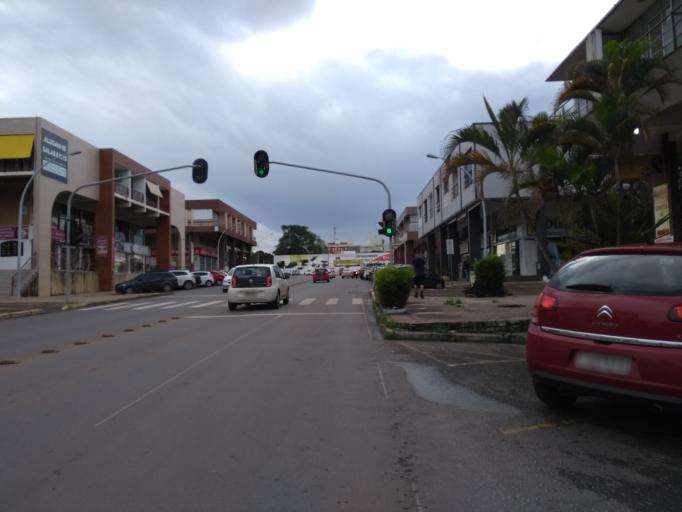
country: BR
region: Federal District
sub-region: Brasilia
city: Brasilia
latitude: -15.7440
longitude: -47.8949
